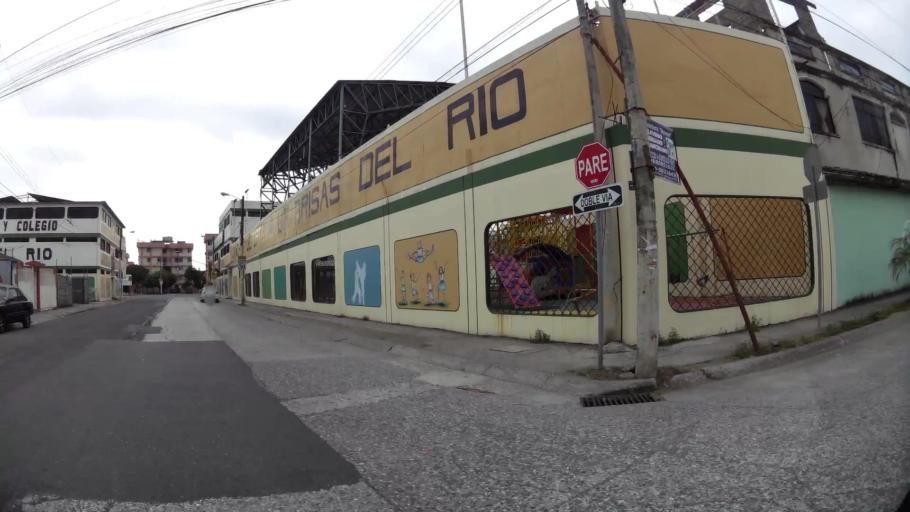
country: EC
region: Guayas
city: Eloy Alfaro
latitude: -2.1296
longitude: -79.8845
